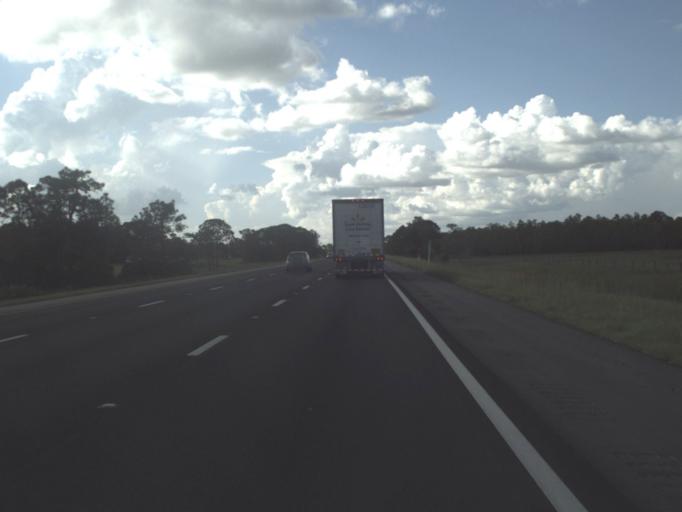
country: US
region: Florida
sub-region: Lee County
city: Burnt Store Marina
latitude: 26.8254
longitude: -81.9482
